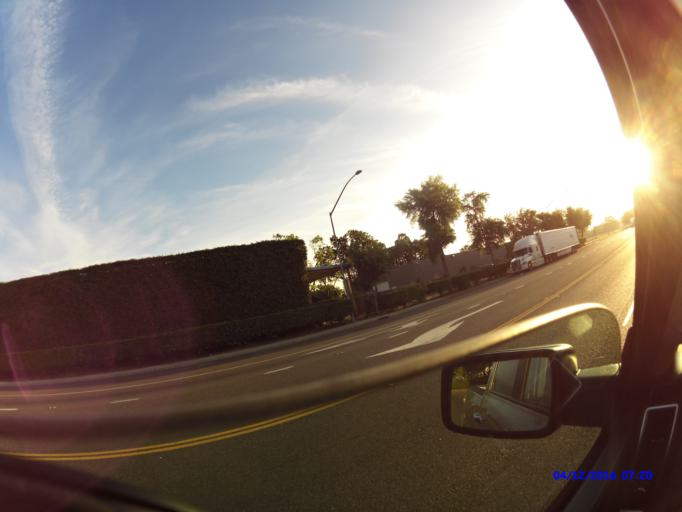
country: US
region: California
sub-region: Stanislaus County
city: Modesto
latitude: 37.6373
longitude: -120.9888
